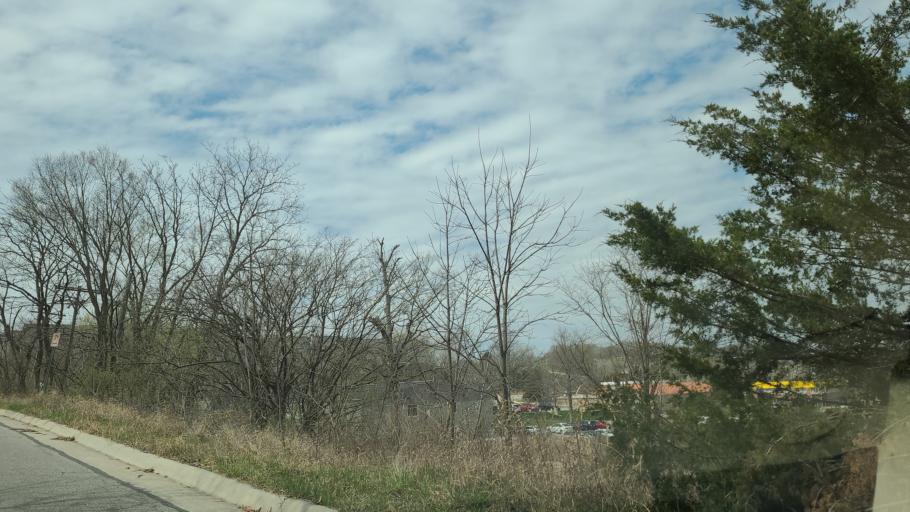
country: US
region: Kansas
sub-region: Douglas County
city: Lawrence
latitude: 38.9715
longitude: -95.2549
